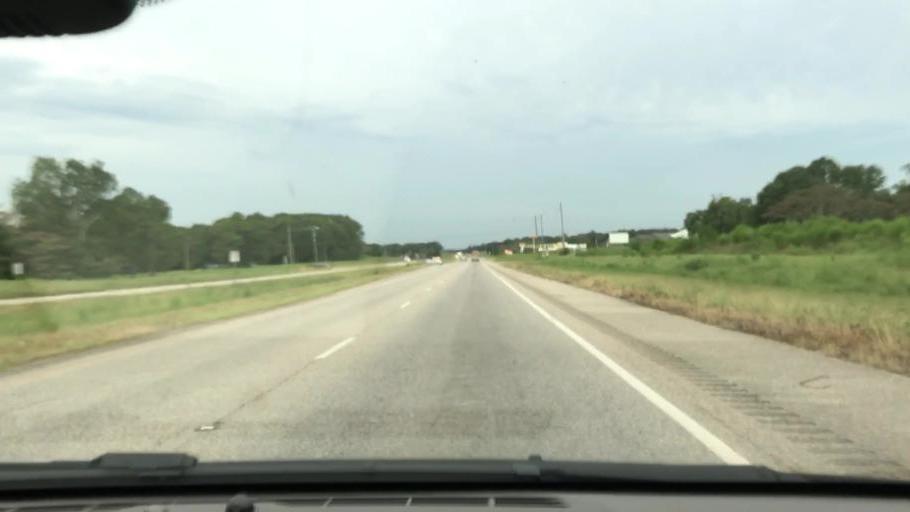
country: US
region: Alabama
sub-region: Houston County
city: Ashford
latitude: 31.1776
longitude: -85.2431
